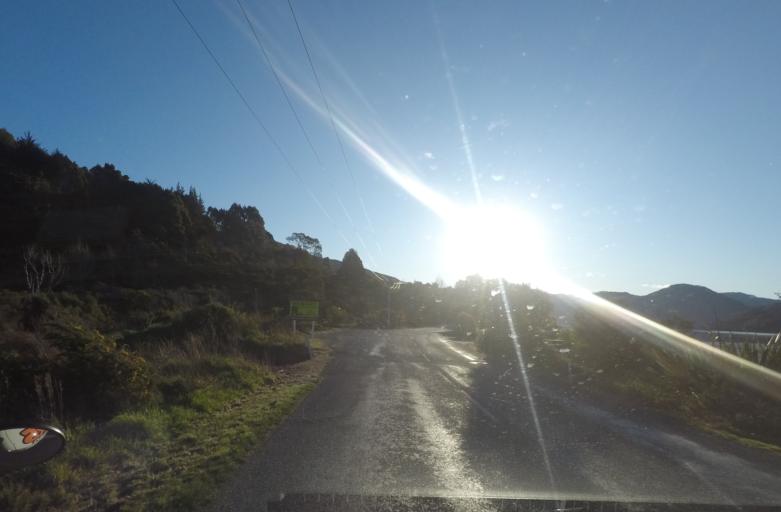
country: NZ
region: Marlborough
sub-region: Marlborough District
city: Picton
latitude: -41.2924
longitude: 173.8207
